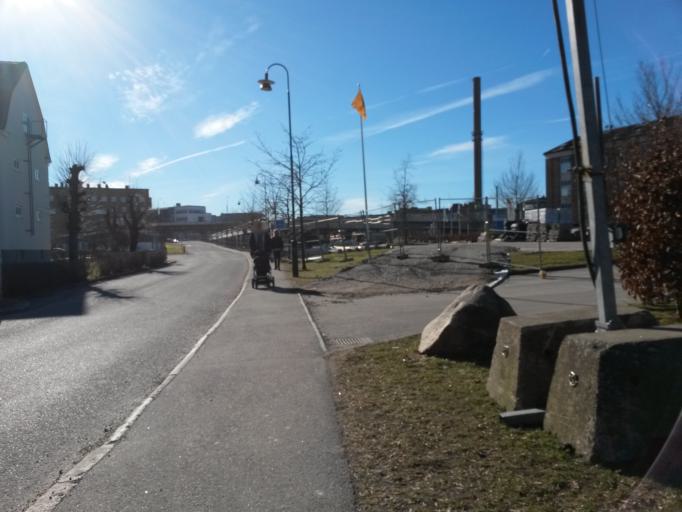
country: SE
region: Vaestra Goetaland
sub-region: Boras Kommun
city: Boras
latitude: 57.7282
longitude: 12.9411
